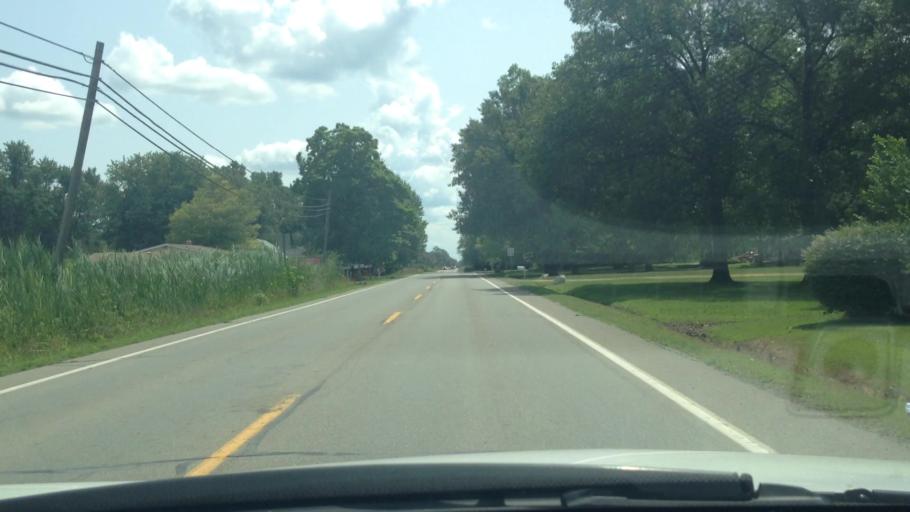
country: US
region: Michigan
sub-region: Wayne County
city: Woodhaven
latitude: 42.1760
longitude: -83.3059
